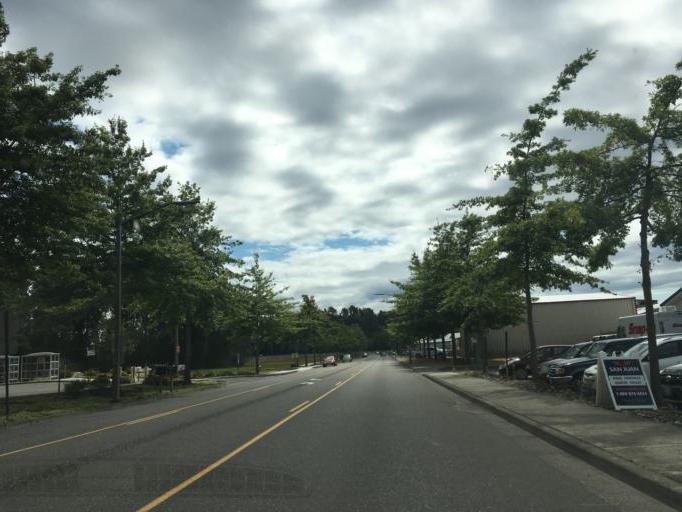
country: US
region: Washington
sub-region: Whatcom County
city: Marietta-Alderwood
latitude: 48.7926
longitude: -122.5306
